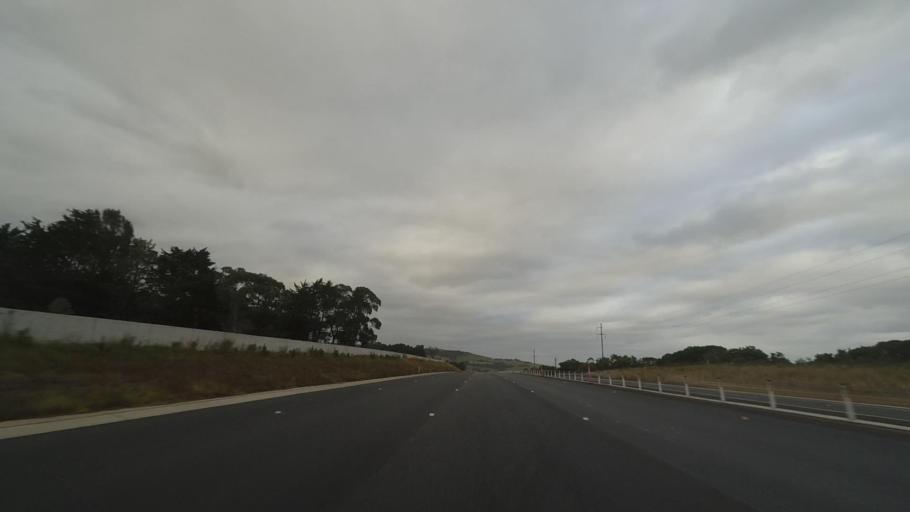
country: AU
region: New South Wales
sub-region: Kiama
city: Gerringong
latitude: -34.7444
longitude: 150.8161
